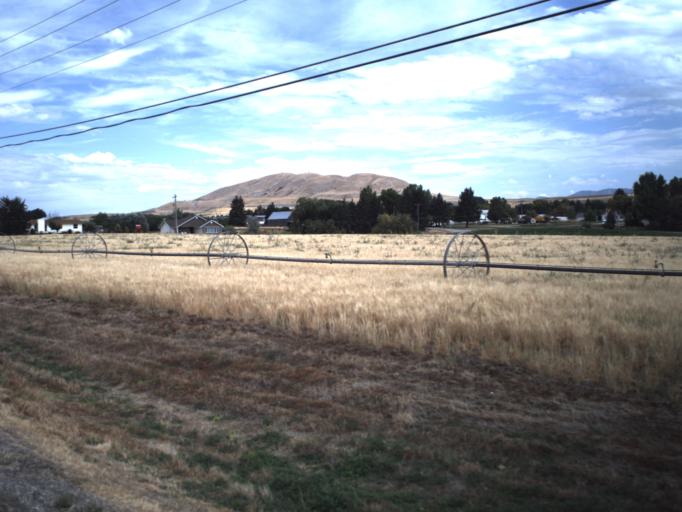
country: US
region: Utah
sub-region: Cache County
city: Benson
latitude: 41.8565
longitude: -112.0000
